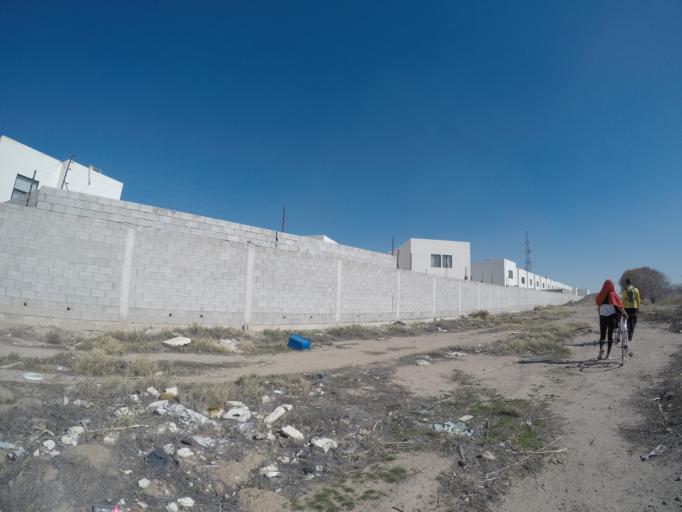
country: US
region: Texas
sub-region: El Paso County
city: Socorro
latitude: 31.6610
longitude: -106.3747
